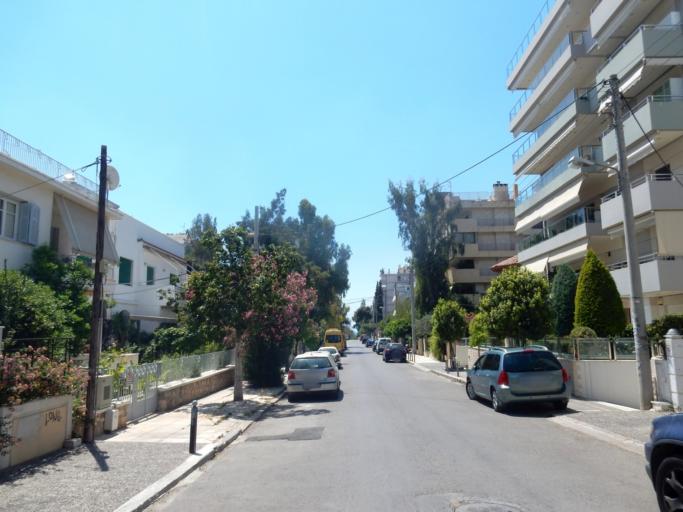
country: GR
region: Attica
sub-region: Nomarchia Athinas
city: Palaio Faliro
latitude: 37.9267
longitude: 23.6970
